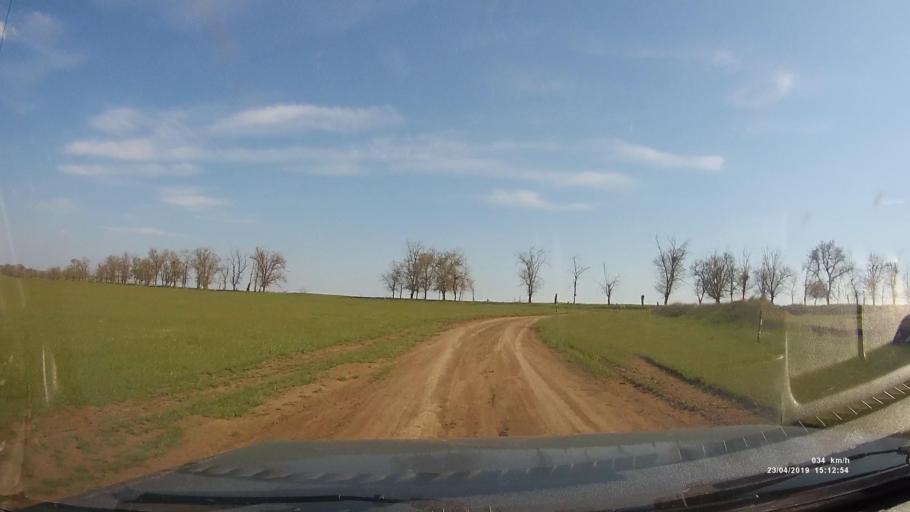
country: RU
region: Rostov
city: Remontnoye
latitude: 46.5408
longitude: 42.9526
